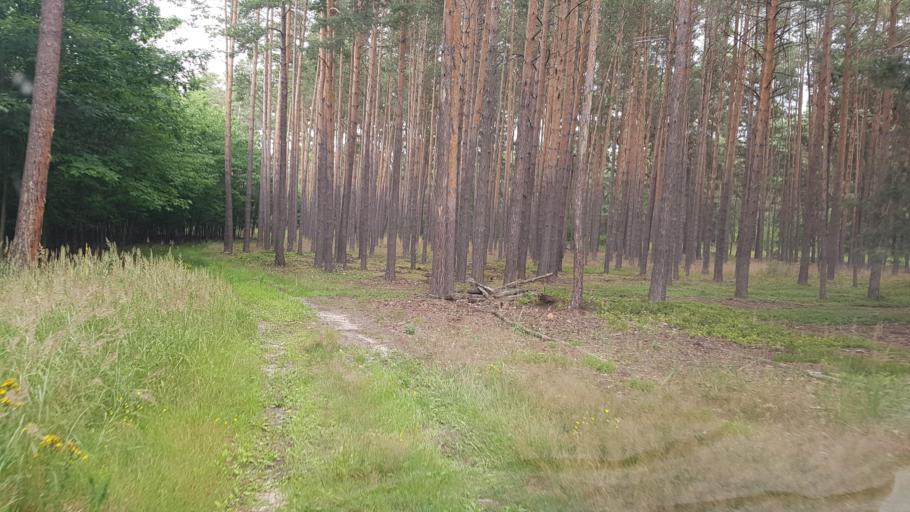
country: DE
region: Brandenburg
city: Crinitz
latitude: 51.7148
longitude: 13.7290
